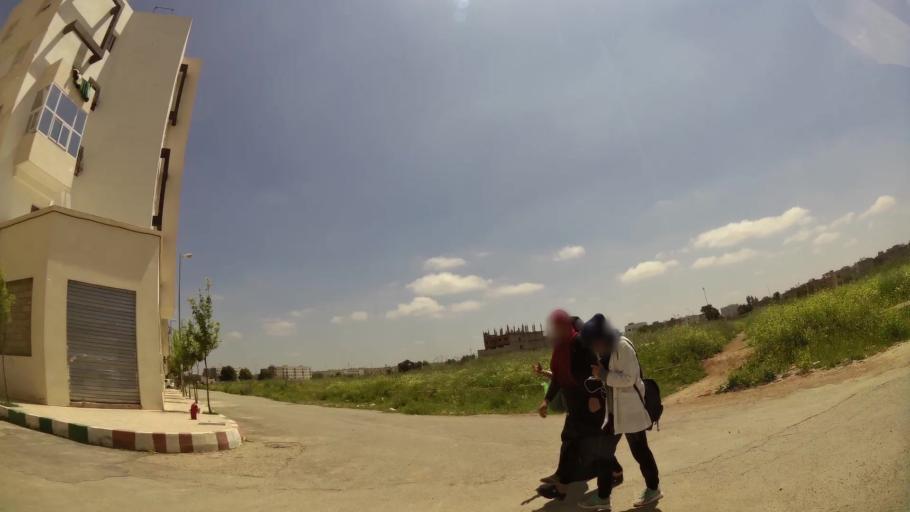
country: MA
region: Fes-Boulemane
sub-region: Fes
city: Fes
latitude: 34.0234
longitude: -5.0433
